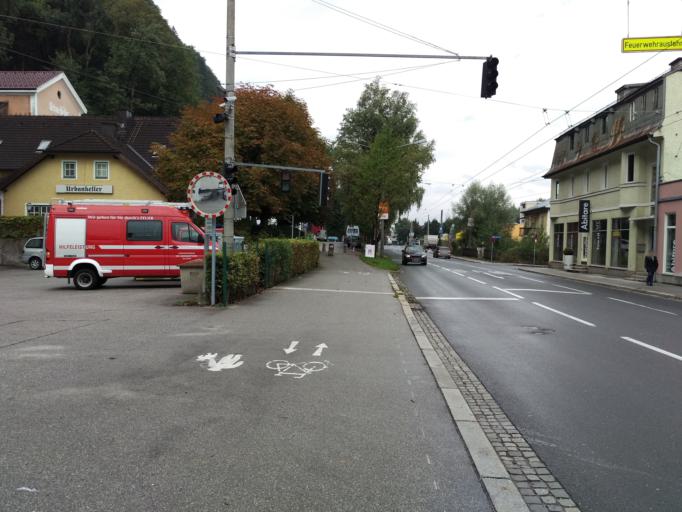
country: AT
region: Salzburg
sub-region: Salzburg Stadt
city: Salzburg
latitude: 47.8075
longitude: 13.0614
